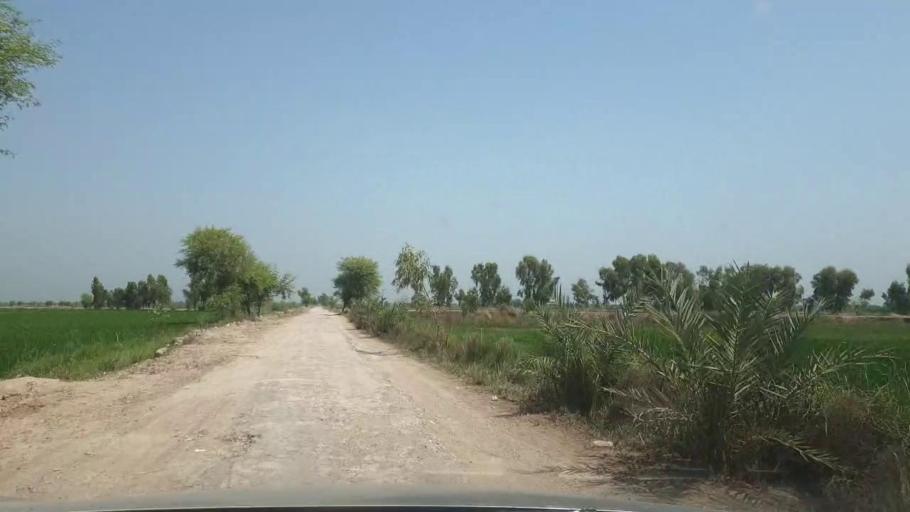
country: PK
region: Sindh
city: Warah
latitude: 27.5091
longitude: 67.7660
